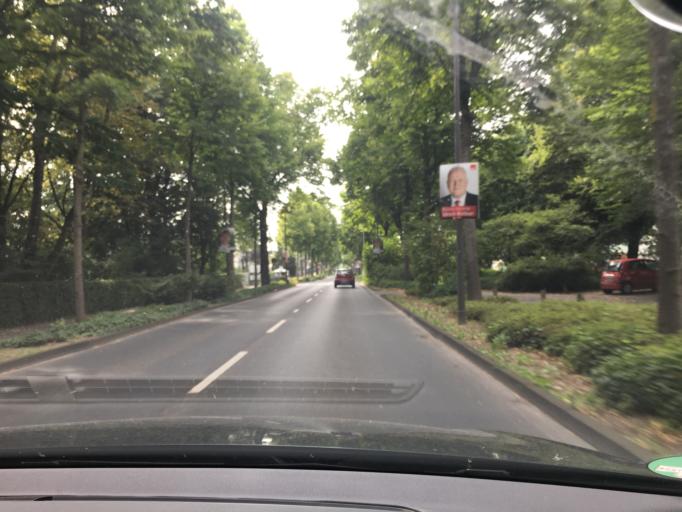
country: DE
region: North Rhine-Westphalia
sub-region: Regierungsbezirk Koln
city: Bonn
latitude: 50.7562
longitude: 7.0678
